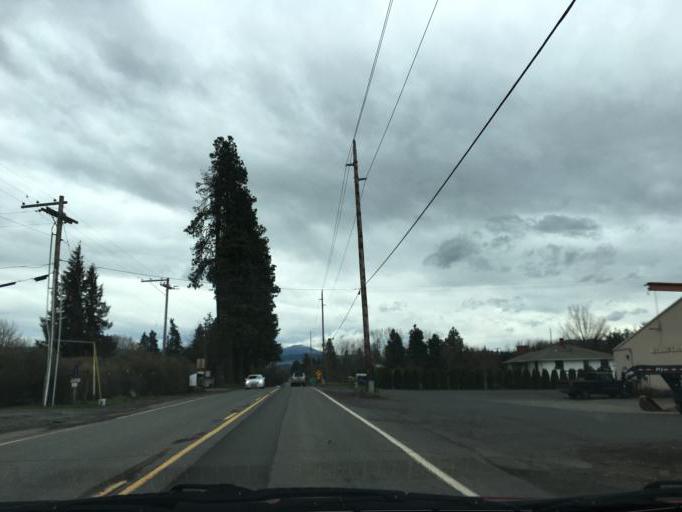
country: US
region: Oregon
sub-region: Hood River County
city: Hood River
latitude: 45.6805
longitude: -121.5290
